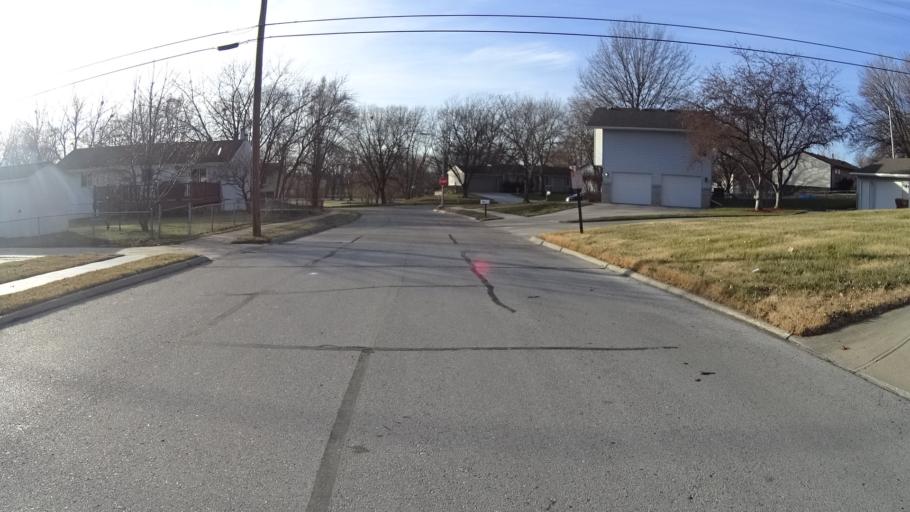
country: US
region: Nebraska
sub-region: Sarpy County
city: La Vista
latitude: 41.1861
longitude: -95.9971
